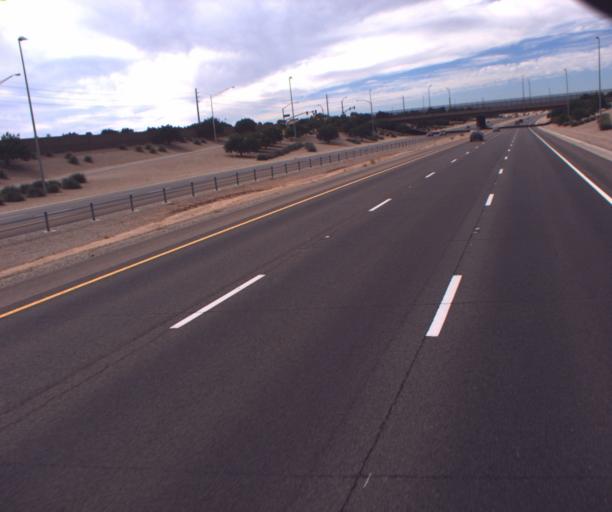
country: US
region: Arizona
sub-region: Maricopa County
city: Gilbert
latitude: 33.3281
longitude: -111.7185
